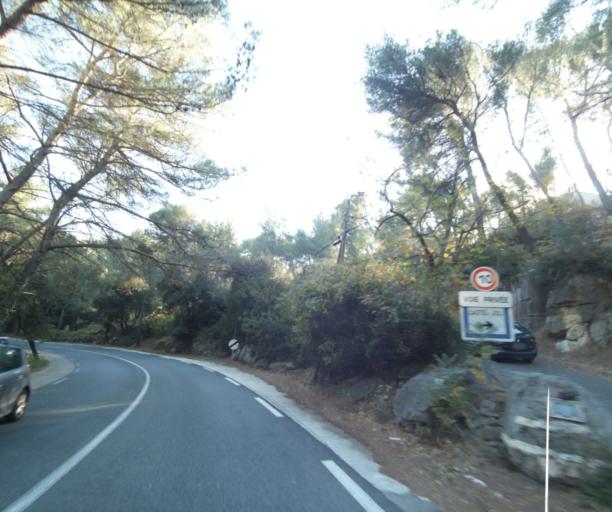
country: FR
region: Provence-Alpes-Cote d'Azur
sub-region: Departement des Bouches-du-Rhone
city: La Ciotat
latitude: 43.1990
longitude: 5.5897
